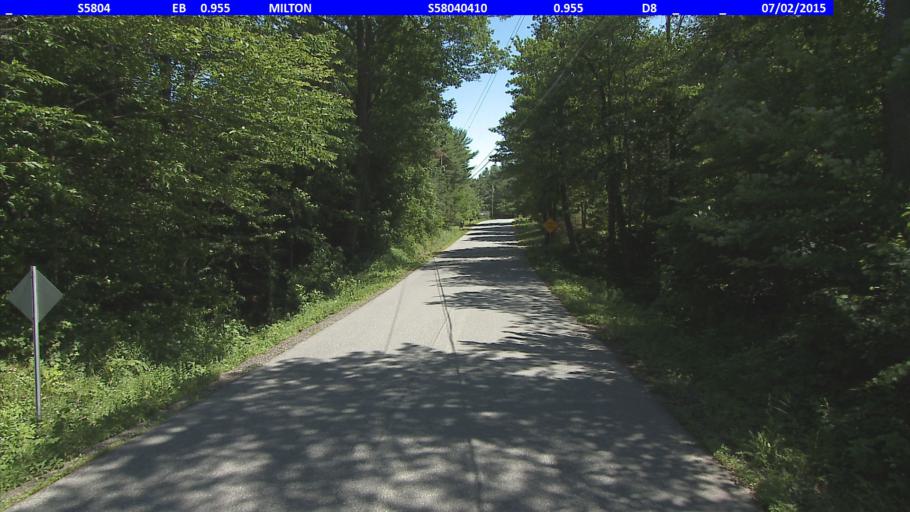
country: US
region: Vermont
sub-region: Chittenden County
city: Milton
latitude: 44.6568
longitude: -73.1544
